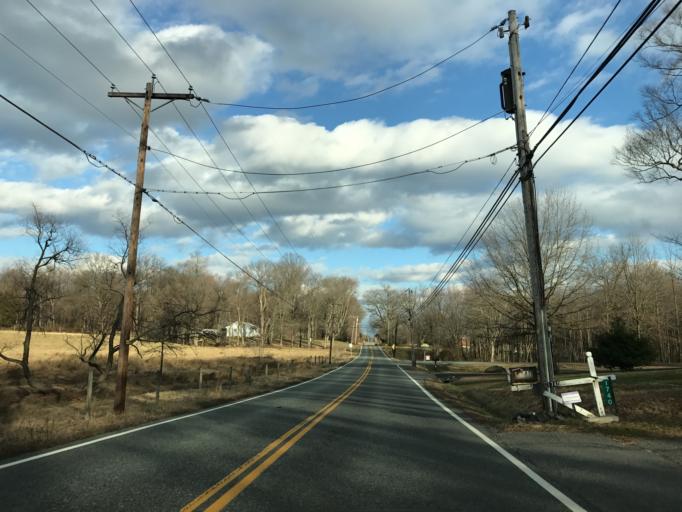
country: US
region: Maryland
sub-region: Cecil County
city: North East
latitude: 39.6402
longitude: -75.9993
